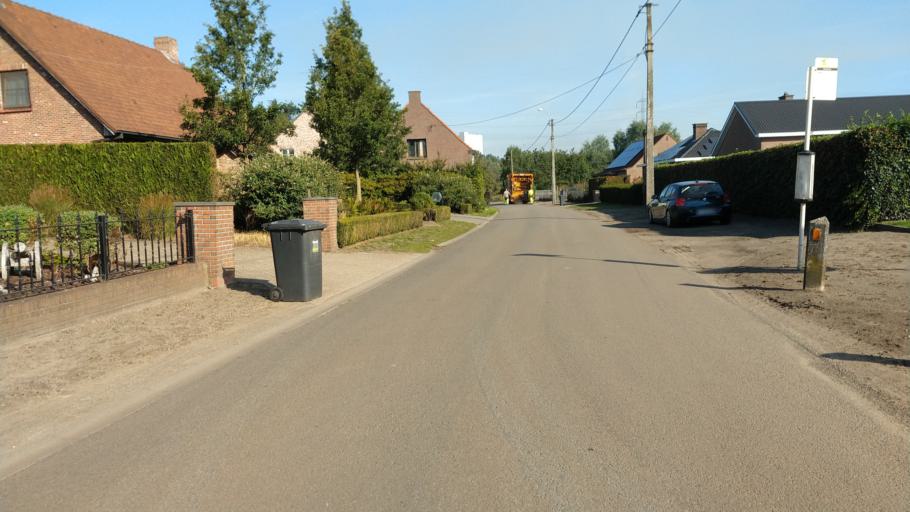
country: BE
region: Flanders
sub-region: Provincie Oost-Vlaanderen
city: Zelzate
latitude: 51.1497
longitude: 3.8119
